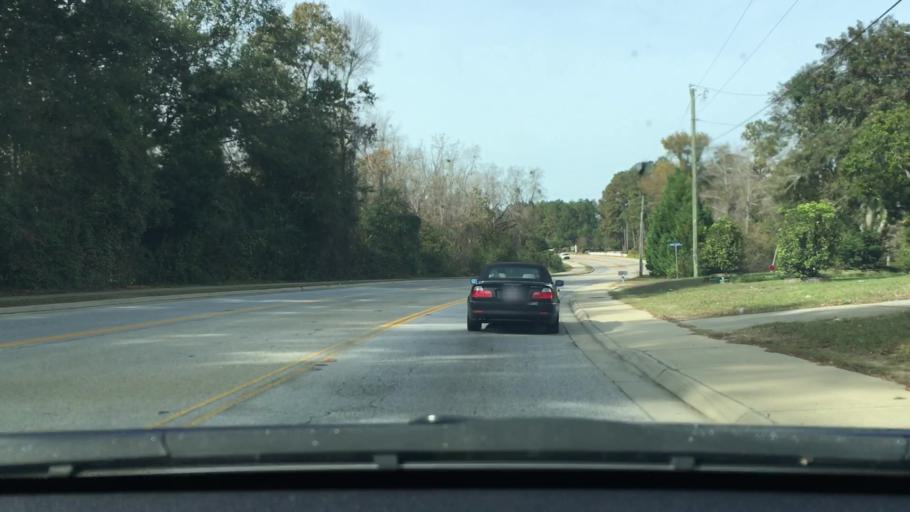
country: US
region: South Carolina
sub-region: Sumter County
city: South Sumter
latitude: 33.9173
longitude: -80.3913
